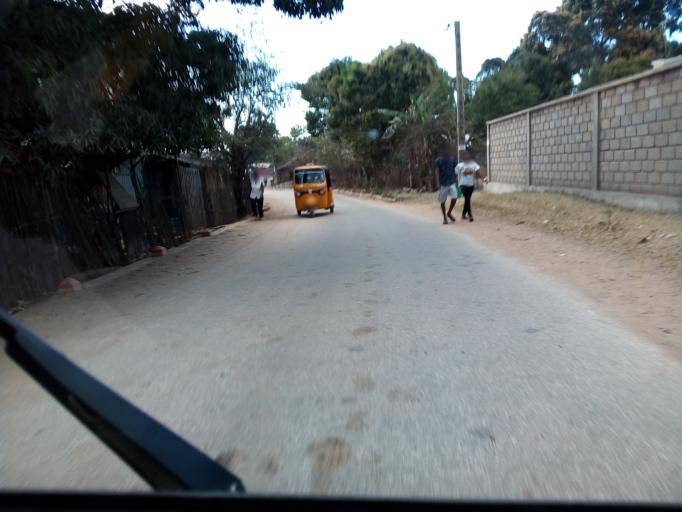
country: MG
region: Boeny
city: Mahajanga
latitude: -15.7059
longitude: 46.3360
